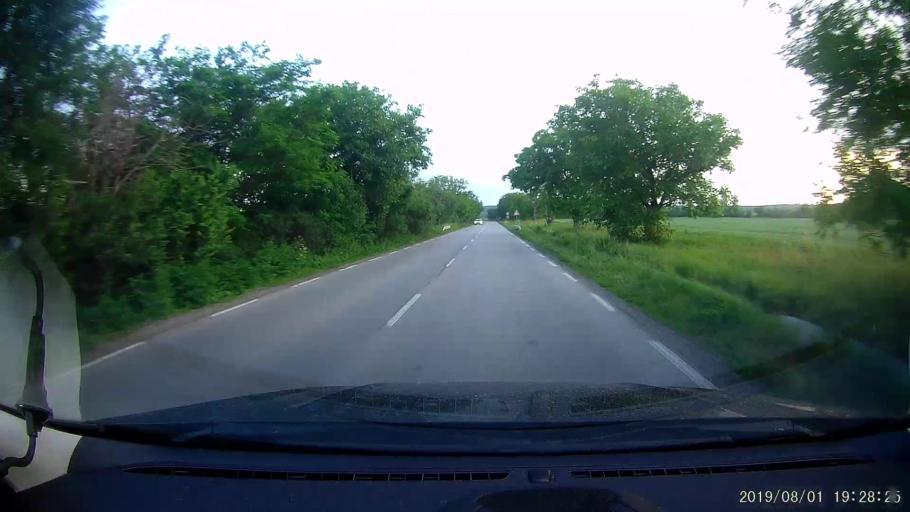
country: BG
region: Burgas
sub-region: Obshtina Sungurlare
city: Sungurlare
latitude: 42.8424
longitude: 26.9173
